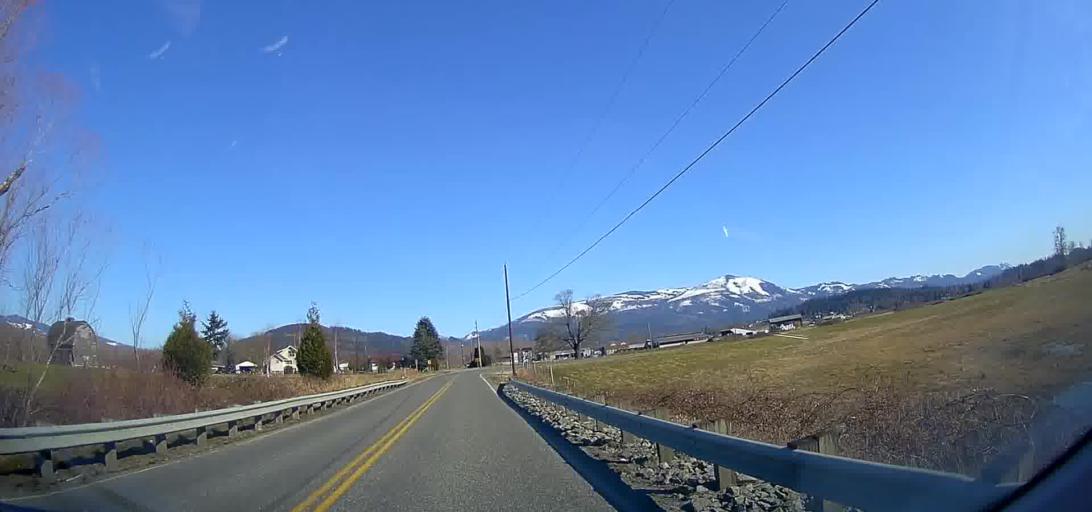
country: US
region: Washington
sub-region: Skagit County
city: Clear Lake
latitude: 48.4680
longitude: -122.2774
